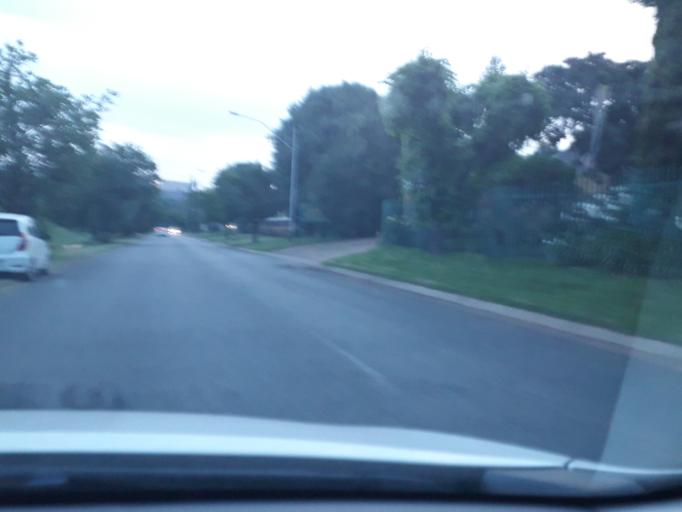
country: ZA
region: Gauteng
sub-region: City of Johannesburg Metropolitan Municipality
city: Johannesburg
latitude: -26.1459
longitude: 27.9995
